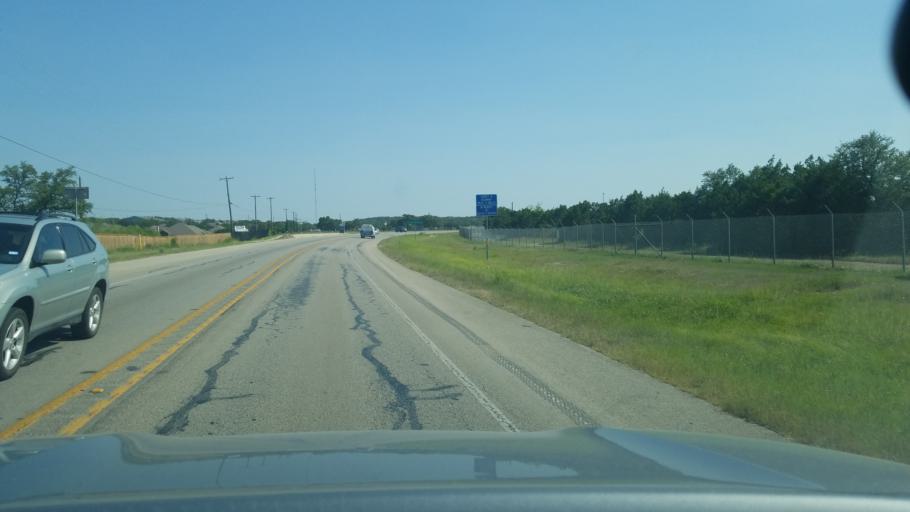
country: US
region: Texas
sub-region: Bexar County
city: Timberwood Park
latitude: 29.7153
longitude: -98.5130
